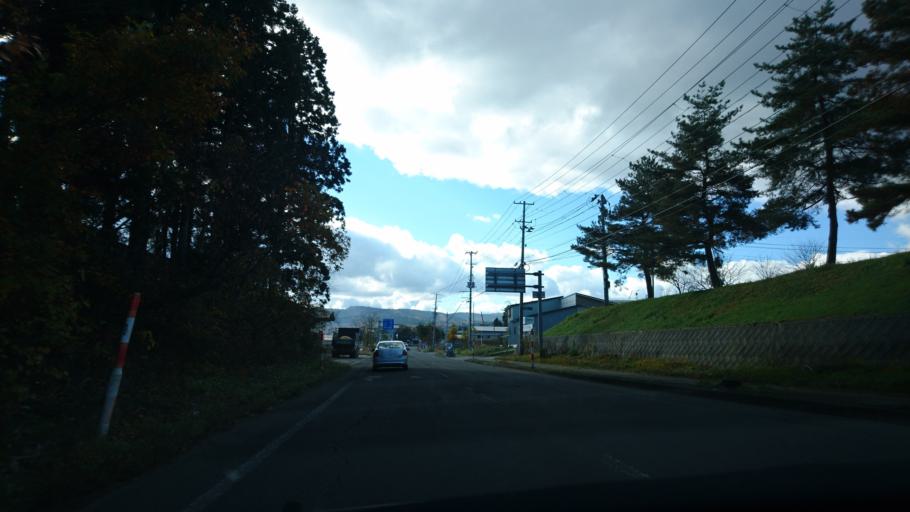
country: JP
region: Akita
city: Yuzawa
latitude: 39.2761
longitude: 140.3966
